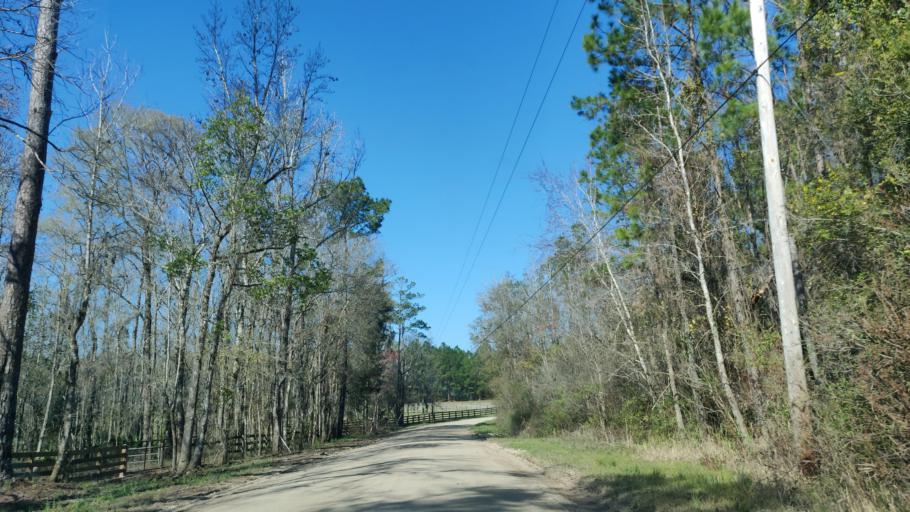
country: US
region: Florida
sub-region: Duval County
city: Baldwin
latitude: 30.1810
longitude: -81.9635
